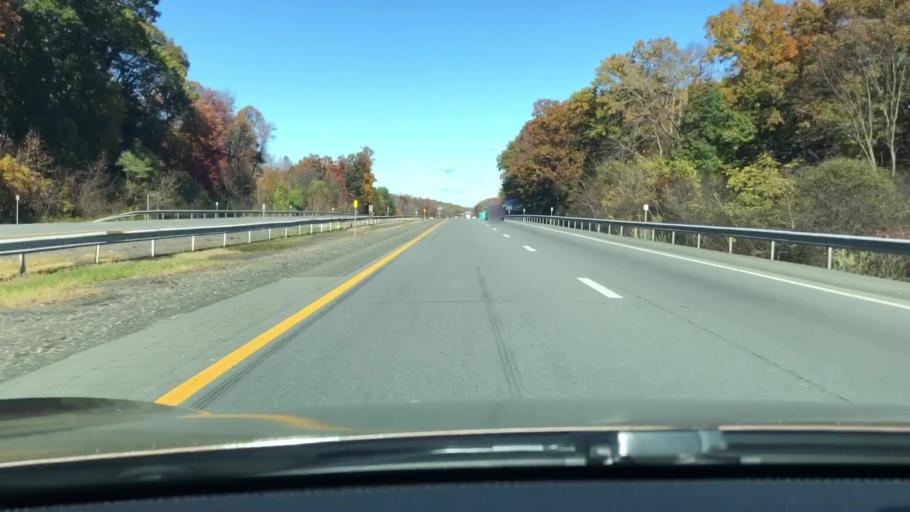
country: US
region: New York
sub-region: Orange County
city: Vails Gate
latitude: 41.4899
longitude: -74.0788
